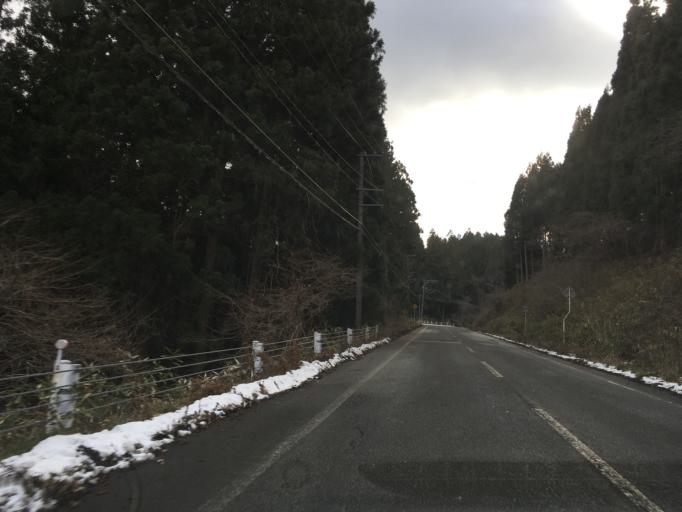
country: JP
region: Miyagi
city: Furukawa
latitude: 38.7900
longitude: 140.8717
